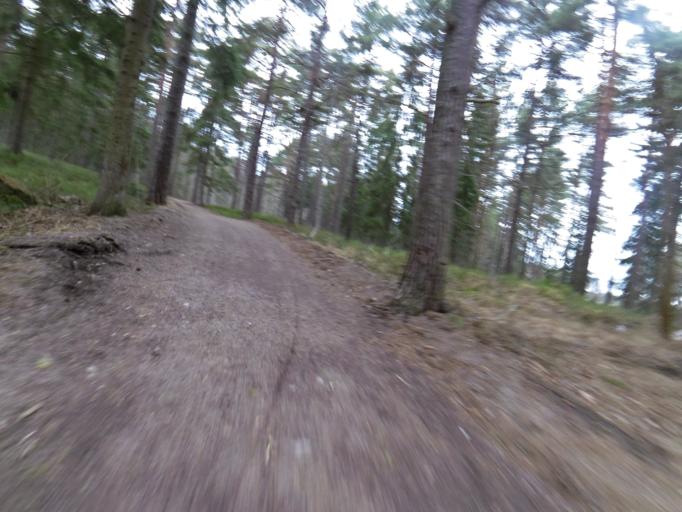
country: SE
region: Gaevleborg
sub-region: Gavle Kommun
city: Gavle
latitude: 60.6623
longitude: 17.1317
